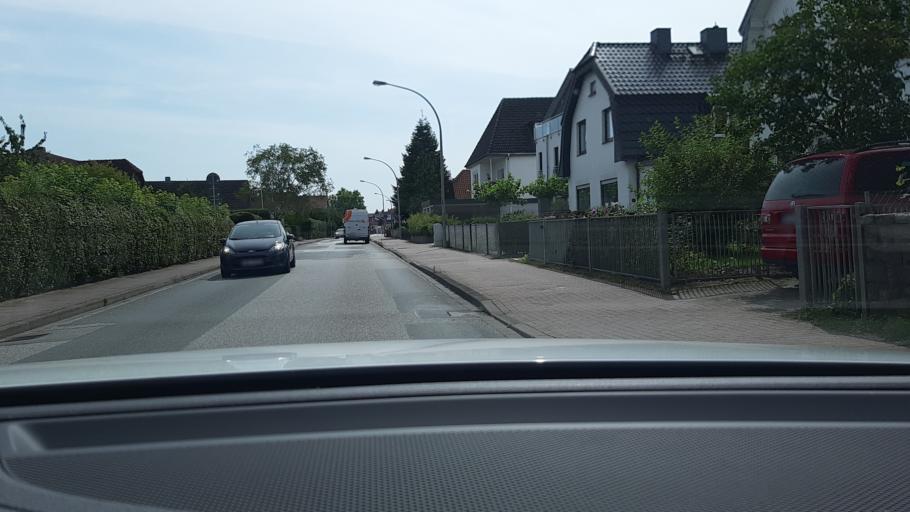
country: DE
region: Schleswig-Holstein
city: Stockelsdorf
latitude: 53.8939
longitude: 10.6512
